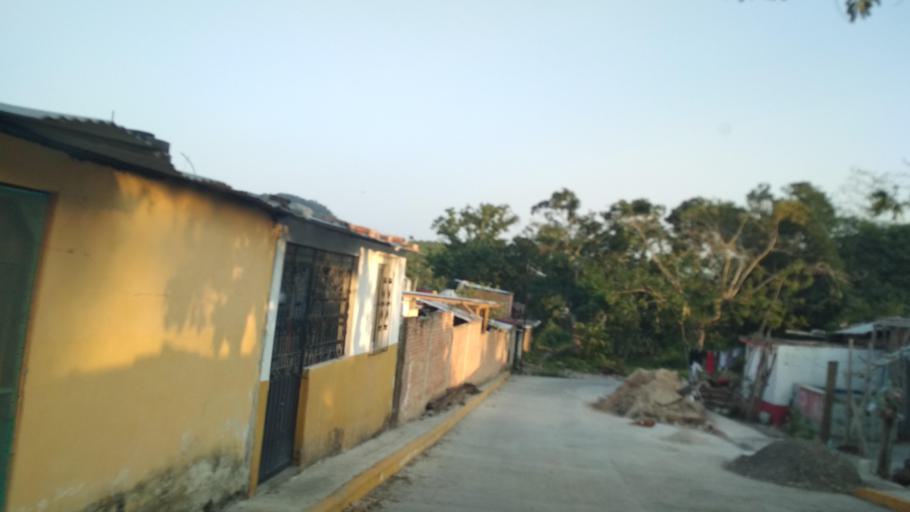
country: MM
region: Shan
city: Taunggyi
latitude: 20.4099
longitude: 97.3368
